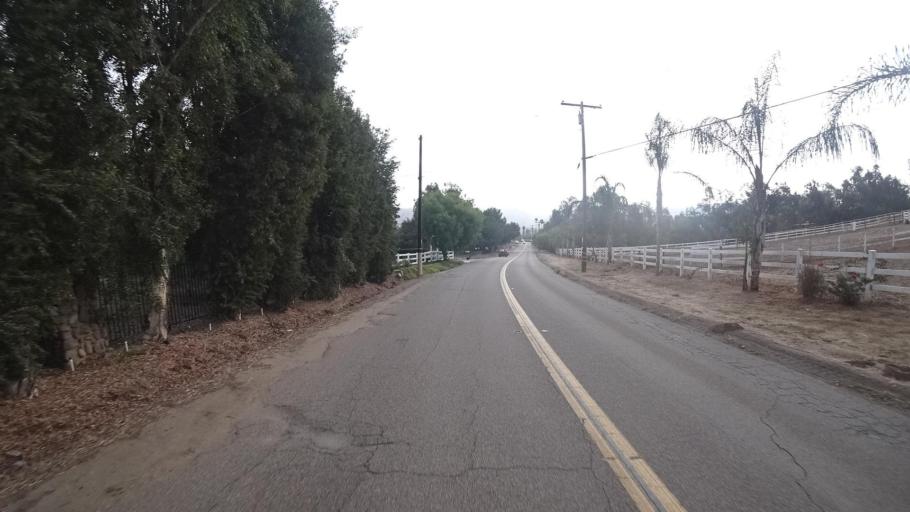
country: US
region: California
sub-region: San Diego County
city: San Marcos
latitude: 33.1798
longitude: -117.1629
